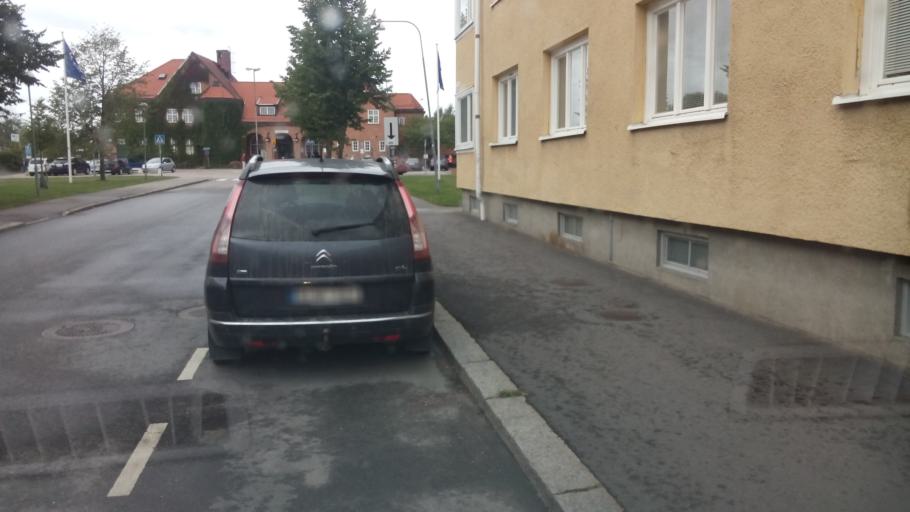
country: SE
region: Soedermanland
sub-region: Nykopings Kommun
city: Nykoping
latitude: 58.7555
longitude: 16.9950
